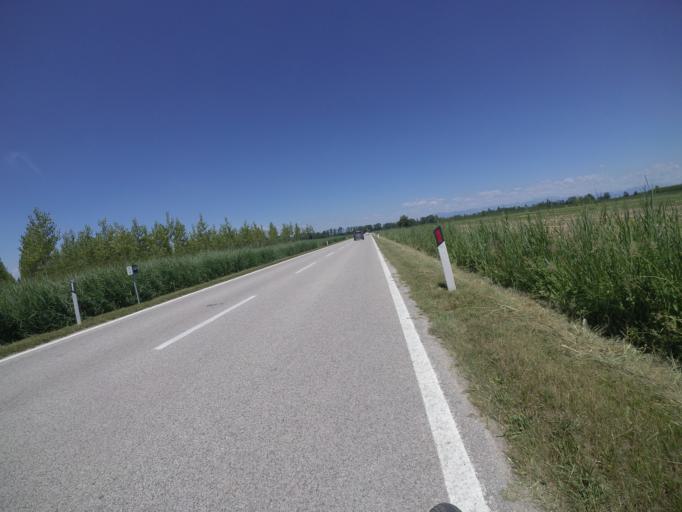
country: IT
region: Friuli Venezia Giulia
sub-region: Provincia di Udine
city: Bertiolo
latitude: 45.9063
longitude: 13.0812
